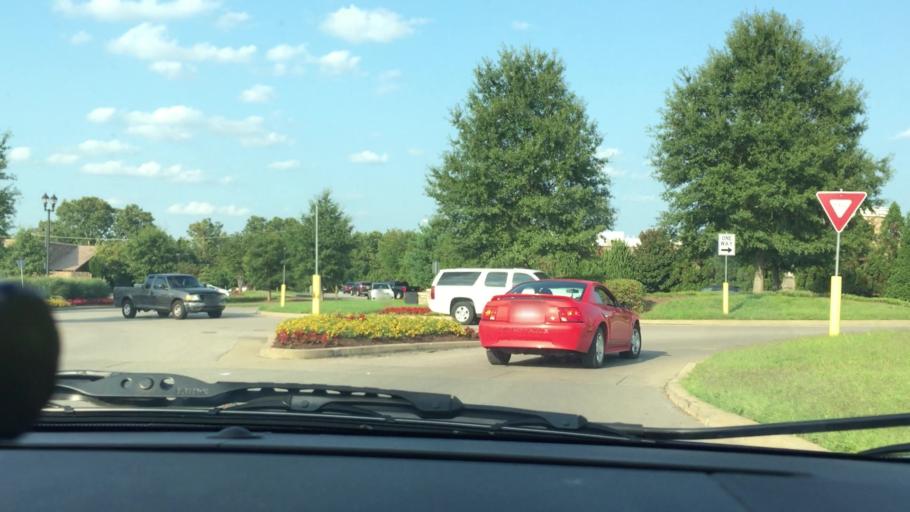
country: US
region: Tennessee
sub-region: Maury County
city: Spring Hill
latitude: 35.7420
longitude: -86.9401
